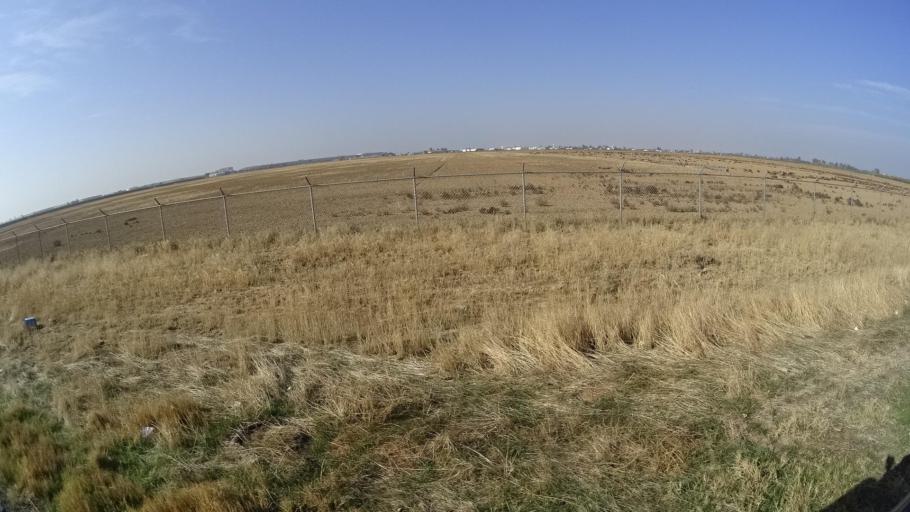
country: US
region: California
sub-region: Kern County
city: Delano
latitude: 35.7418
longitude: -119.2232
